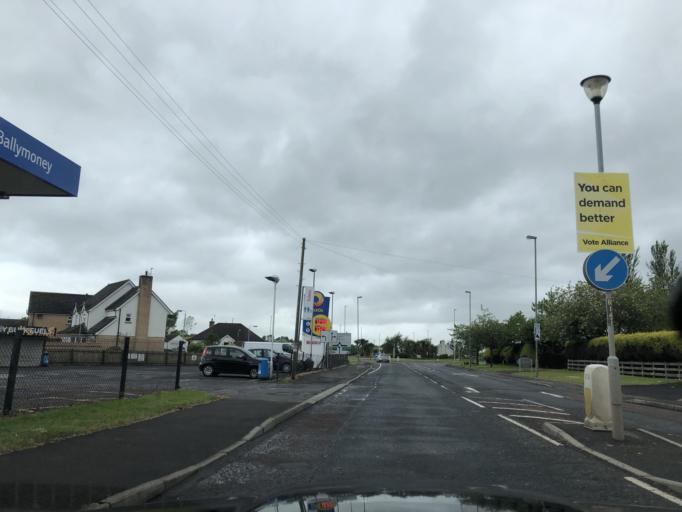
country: GB
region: Northern Ireland
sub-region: Ballymoney District
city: Ballymoney
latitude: 55.0801
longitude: -6.5246
